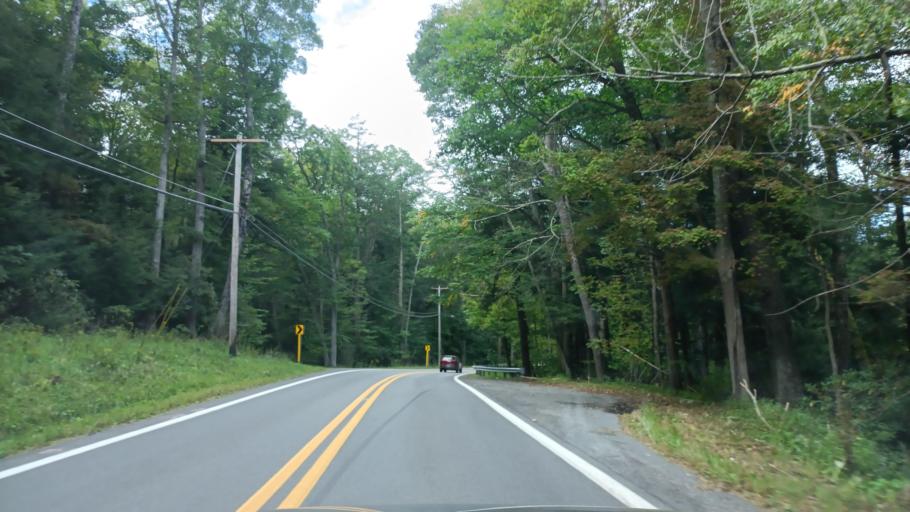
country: US
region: West Virginia
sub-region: Preston County
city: Terra Alta
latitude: 39.3253
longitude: -79.5393
